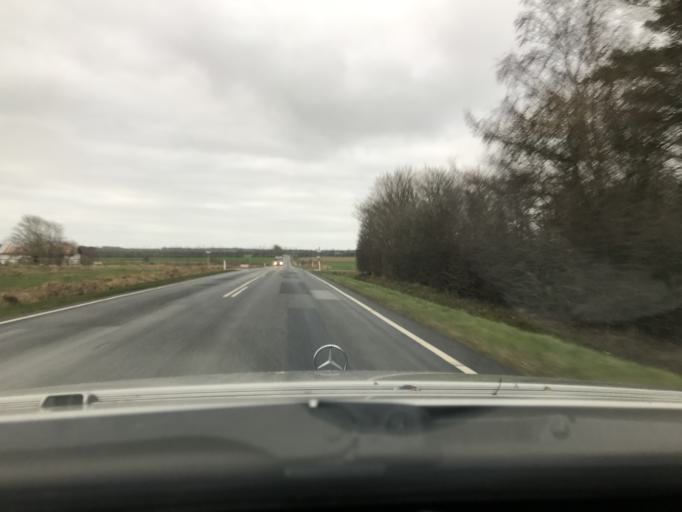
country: DK
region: South Denmark
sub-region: Tonder Kommune
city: Toftlund
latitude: 55.1781
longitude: 9.0187
